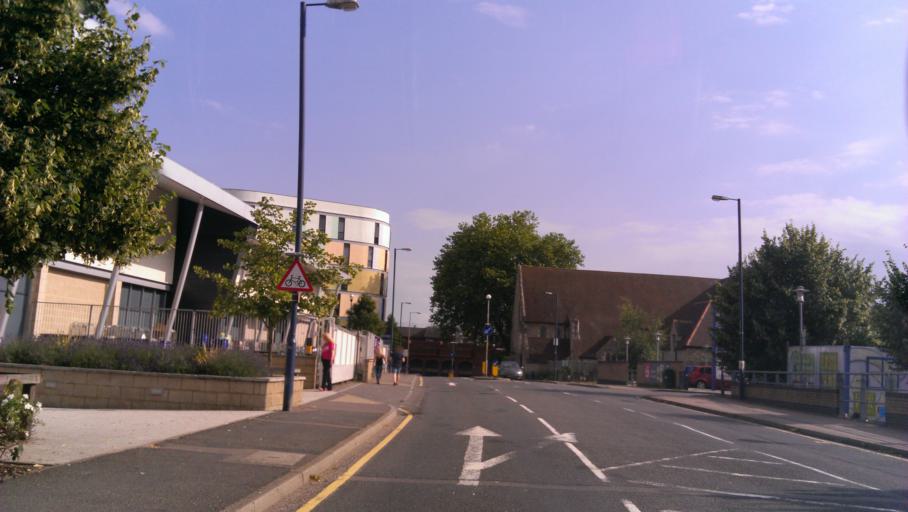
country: GB
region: England
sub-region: Kent
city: Maidstone
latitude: 51.2738
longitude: 0.5162
